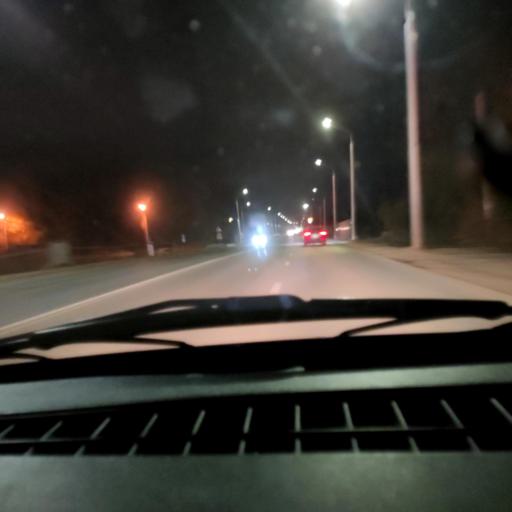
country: RU
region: Bashkortostan
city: Ufa
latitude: 54.7884
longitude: 56.1161
